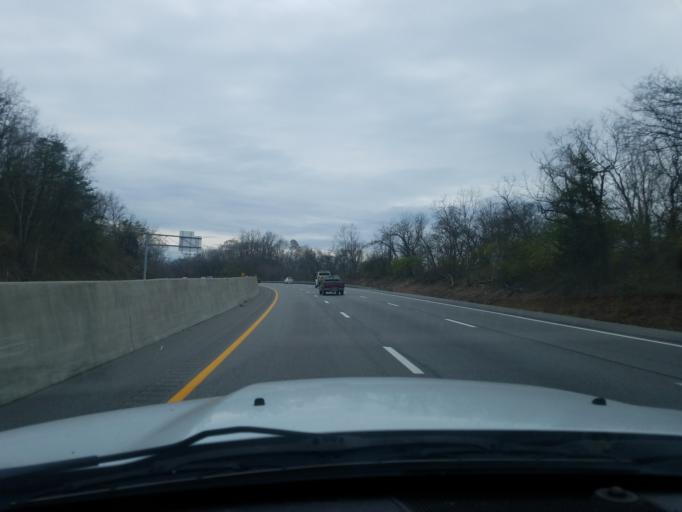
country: US
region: West Virginia
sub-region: Cabell County
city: Pea Ridge
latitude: 38.4096
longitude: -82.3577
